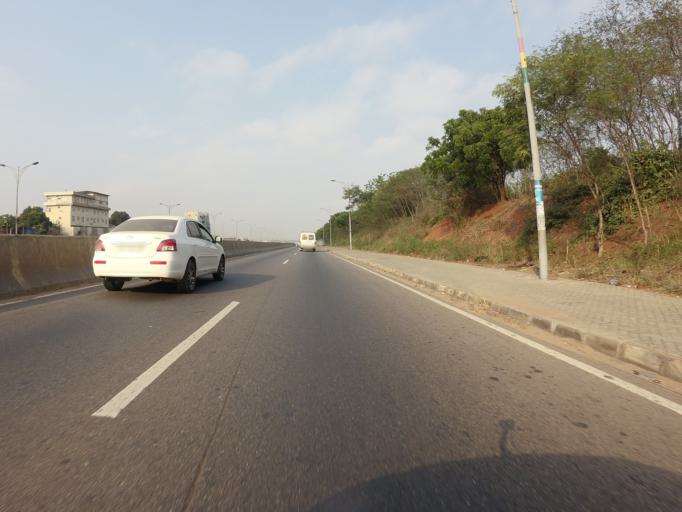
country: GH
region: Greater Accra
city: Dome
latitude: 5.6152
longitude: -0.2163
